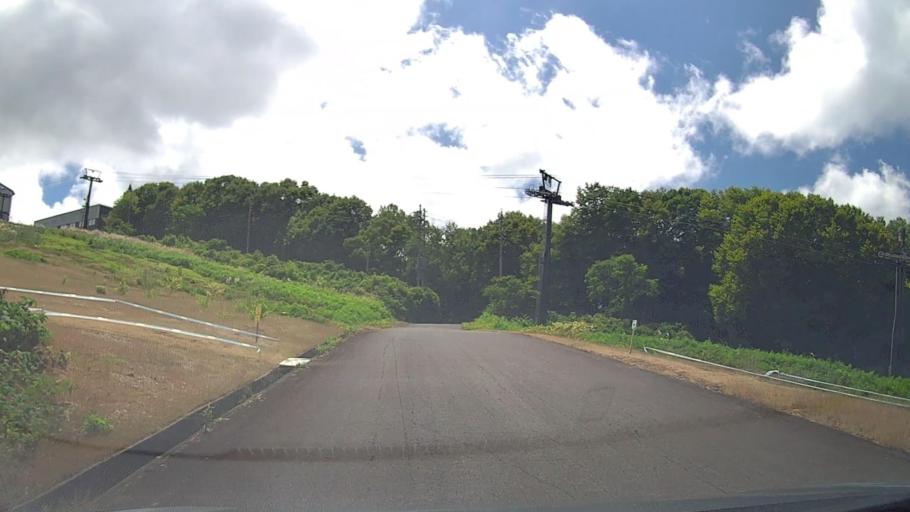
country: JP
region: Nagano
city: Iiyama
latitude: 36.9230
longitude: 138.4752
